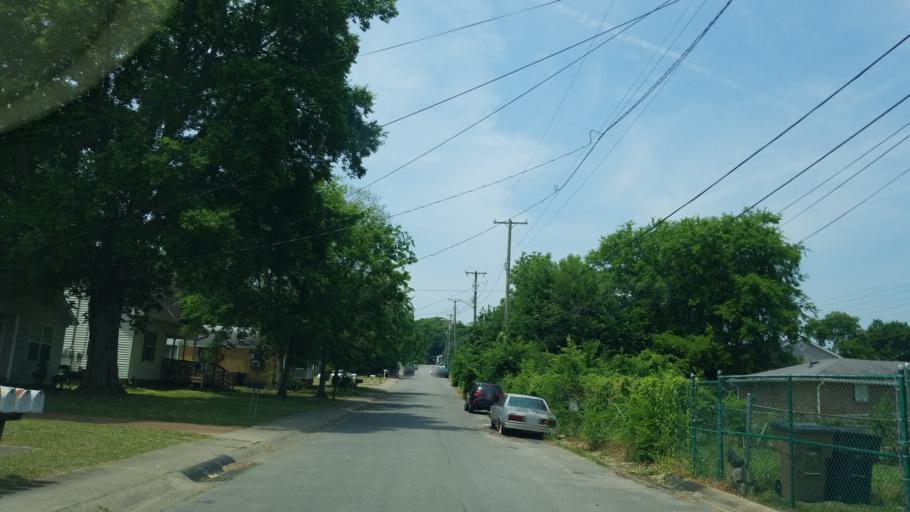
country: US
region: Tennessee
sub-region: Davidson County
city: Nashville
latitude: 36.1625
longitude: -86.8052
